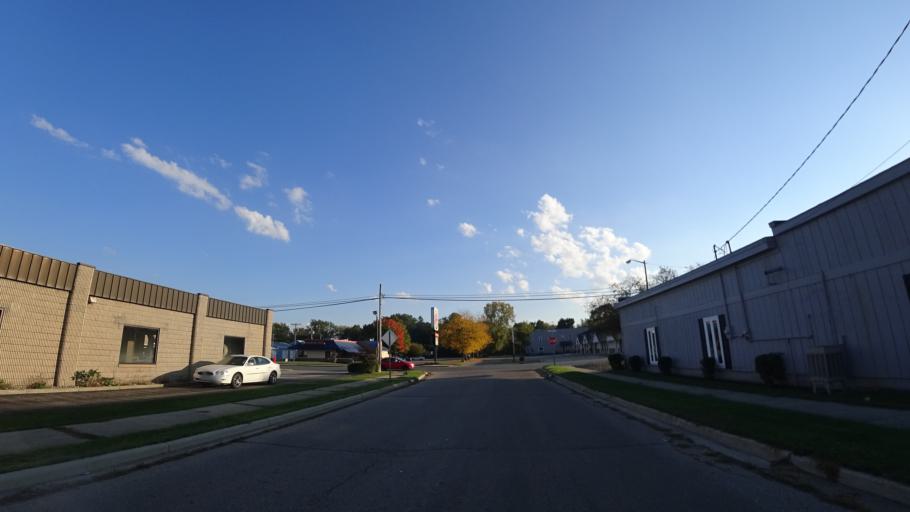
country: US
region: Michigan
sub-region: Saint Joseph County
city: Three Rivers
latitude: 41.9429
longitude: -85.6470
